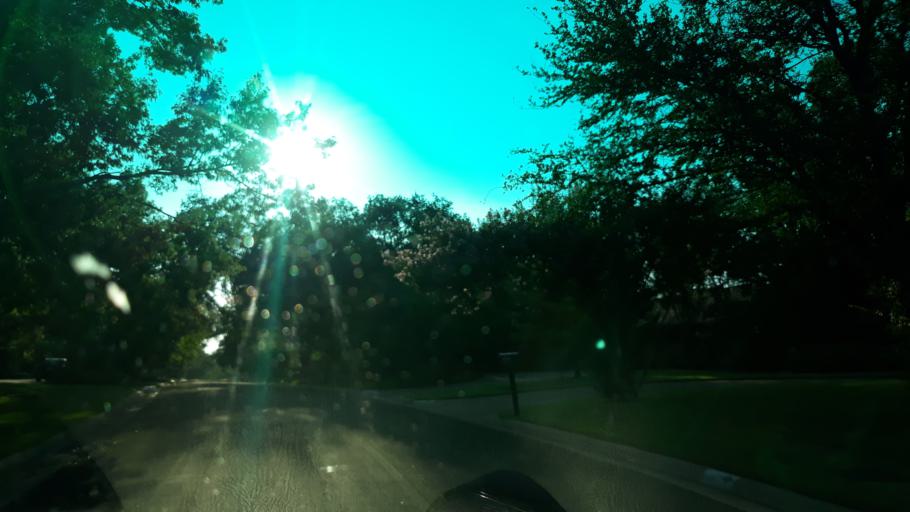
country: US
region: Texas
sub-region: Dallas County
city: Addison
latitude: 32.9475
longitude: -96.7904
